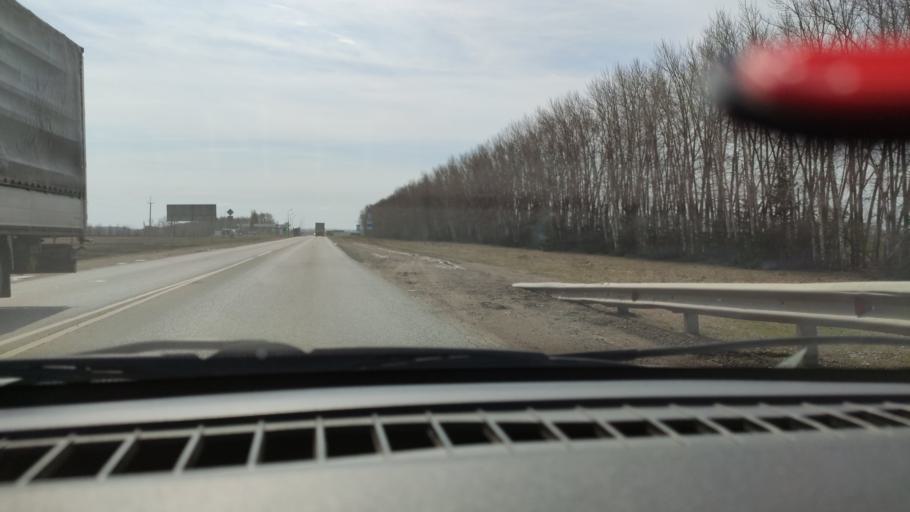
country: RU
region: Bashkortostan
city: Dyurtyuli
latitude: 55.4236
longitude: 54.8077
